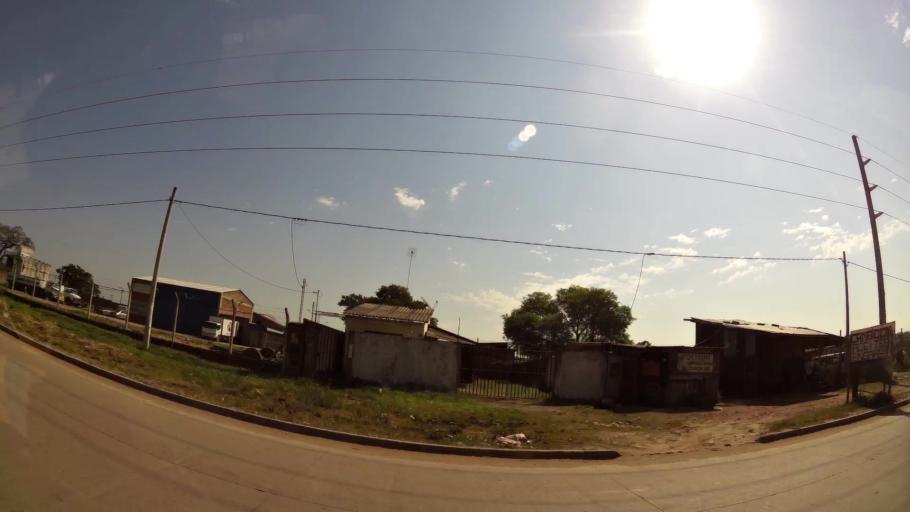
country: BO
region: Santa Cruz
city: Cotoca
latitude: -17.7834
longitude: -63.1081
